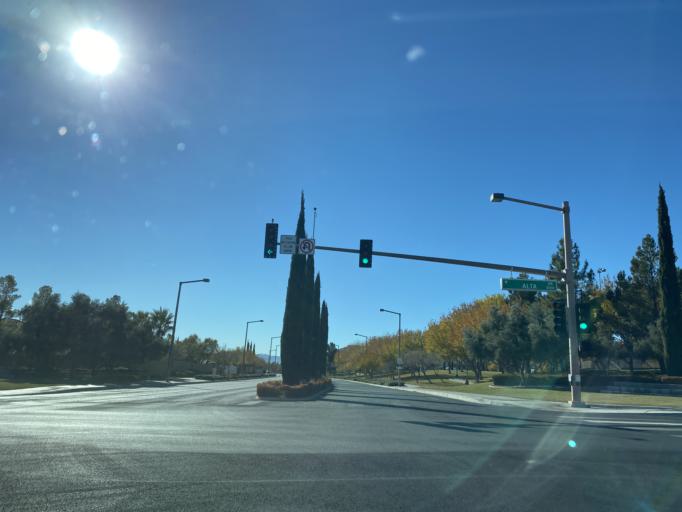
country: US
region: Nevada
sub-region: Clark County
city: Summerlin South
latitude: 36.1708
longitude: -115.3427
